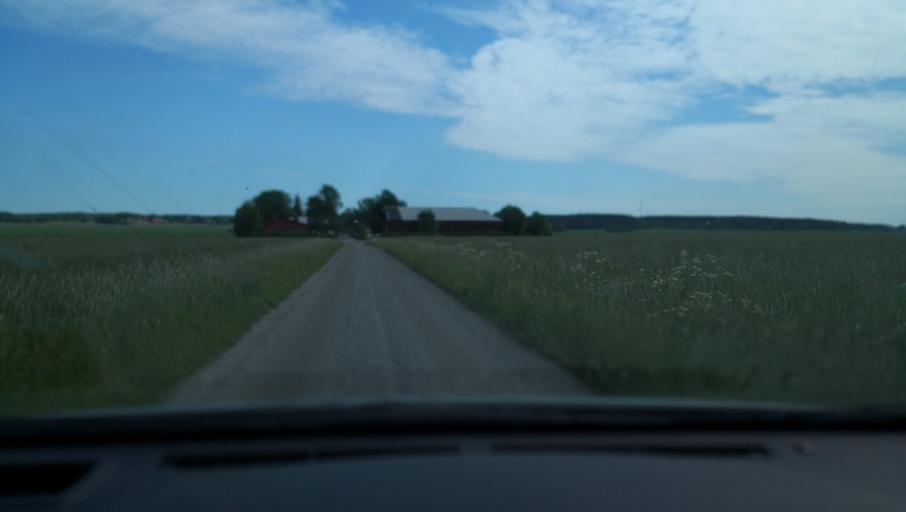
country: SE
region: Uppsala
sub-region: Enkopings Kommun
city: Enkoping
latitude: 59.7069
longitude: 17.1473
